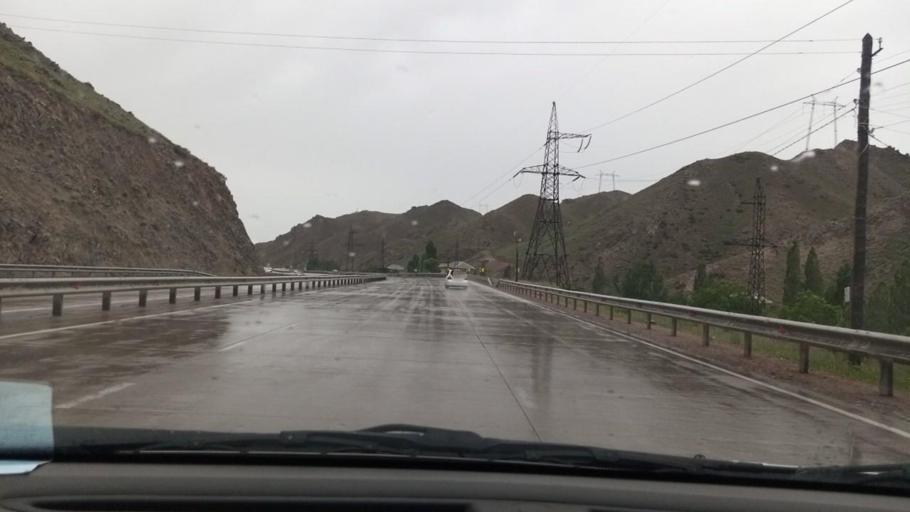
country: TJ
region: Viloyati Sughd
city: Shaydon
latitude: 40.9689
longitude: 70.6556
